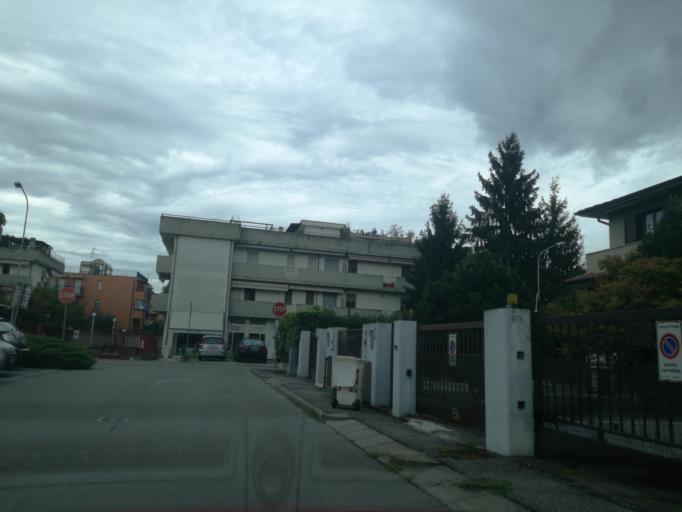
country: IT
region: Lombardy
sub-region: Provincia di Monza e Brianza
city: Ornago
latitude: 45.5999
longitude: 9.4221
